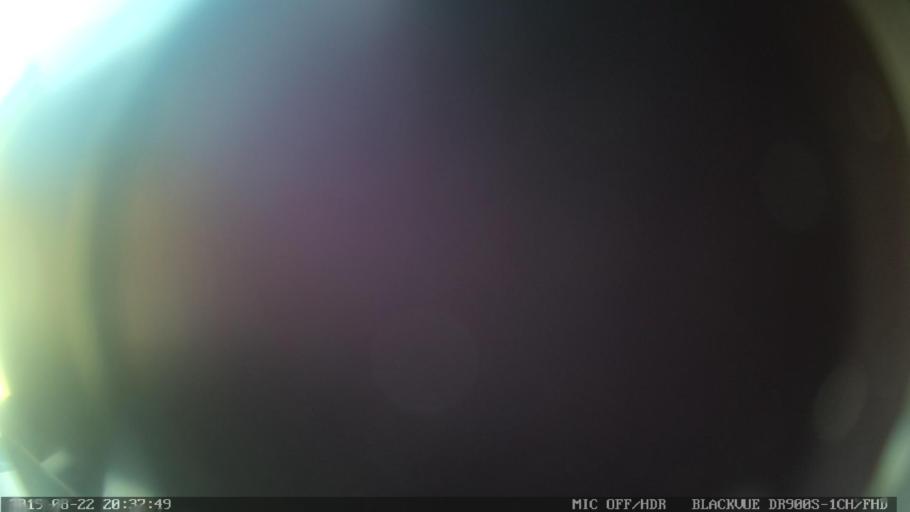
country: PT
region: Portalegre
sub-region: Nisa
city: Nisa
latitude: 39.6780
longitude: -7.7397
